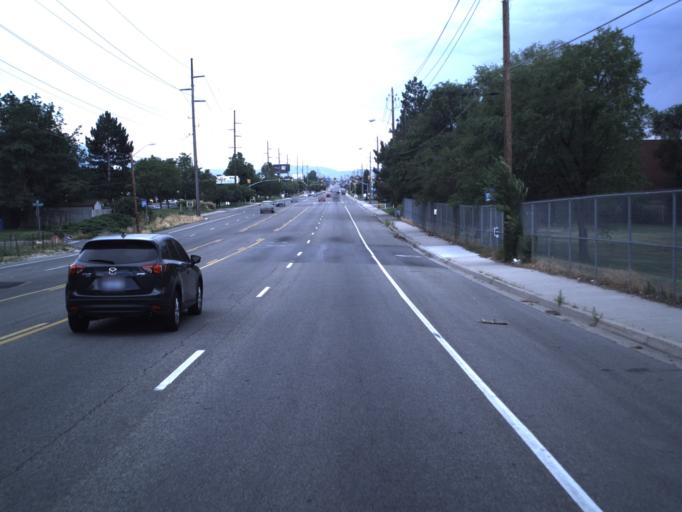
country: US
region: Utah
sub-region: Salt Lake County
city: Murray
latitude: 40.6560
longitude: -111.8660
